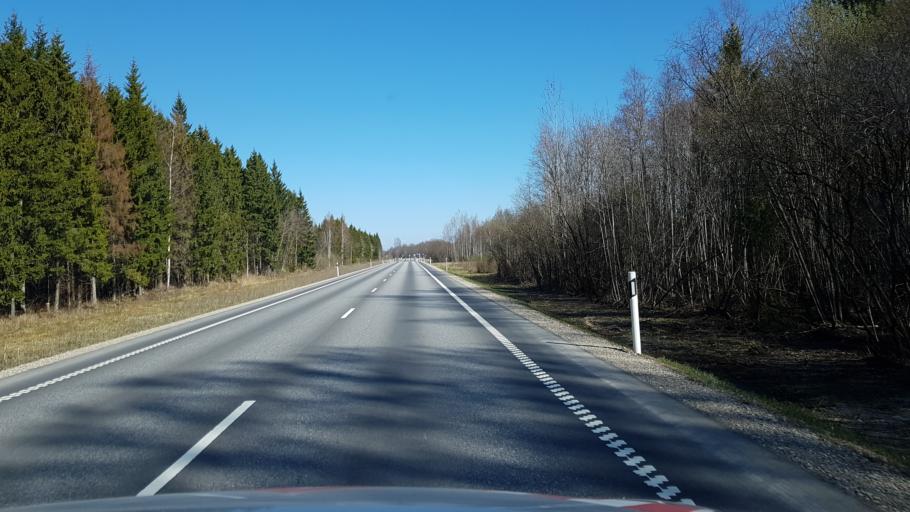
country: EE
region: Jogevamaa
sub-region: Mustvee linn
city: Mustvee
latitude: 58.8471
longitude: 26.8955
